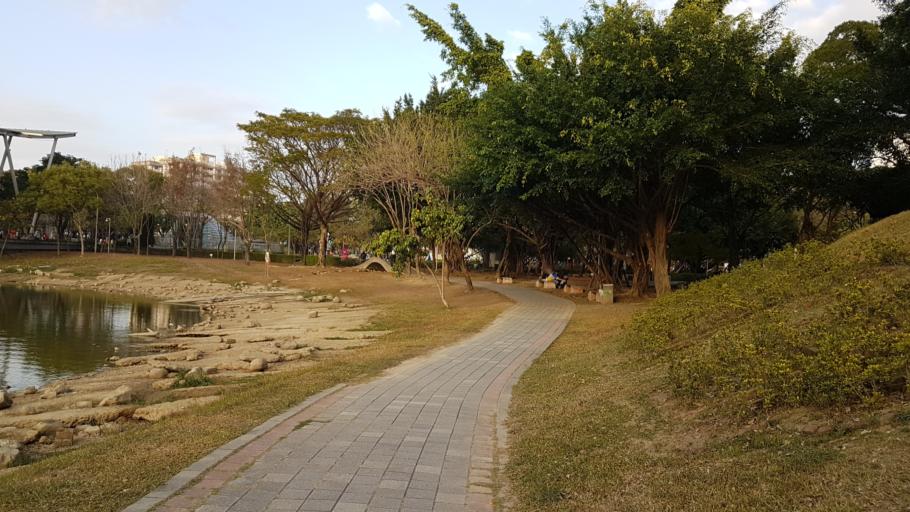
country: TW
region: Taiwan
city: Xinying
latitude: 23.3088
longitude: 120.3146
